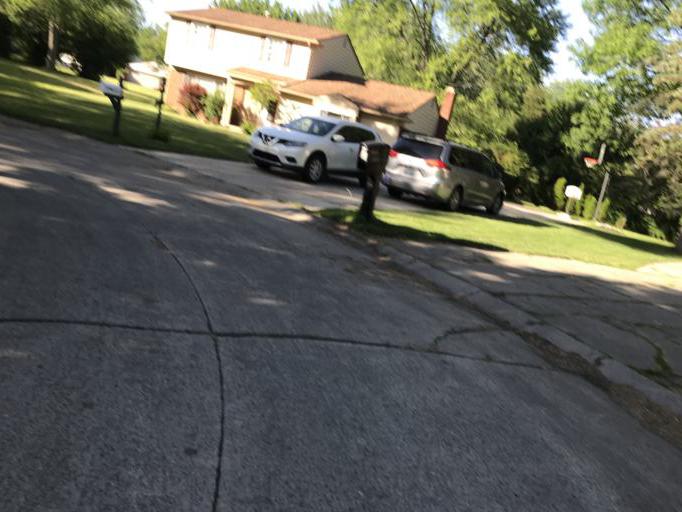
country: US
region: Michigan
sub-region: Oakland County
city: Farmington
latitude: 42.4746
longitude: -83.3335
